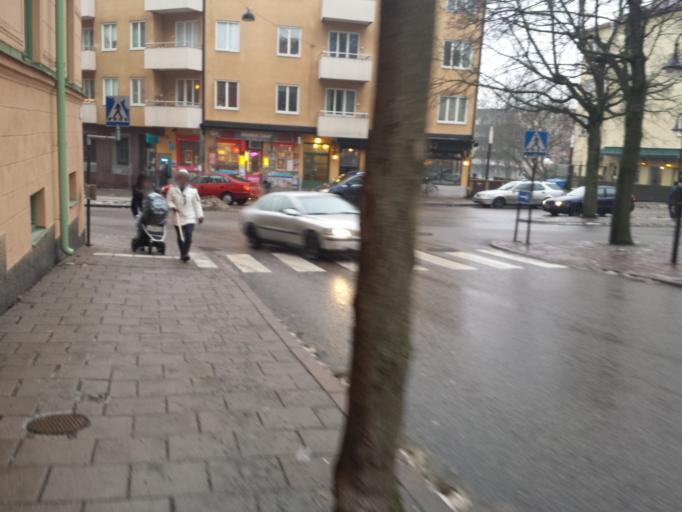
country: SE
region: Stockholm
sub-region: Solna Kommun
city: Solna
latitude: 59.3647
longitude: 17.9950
